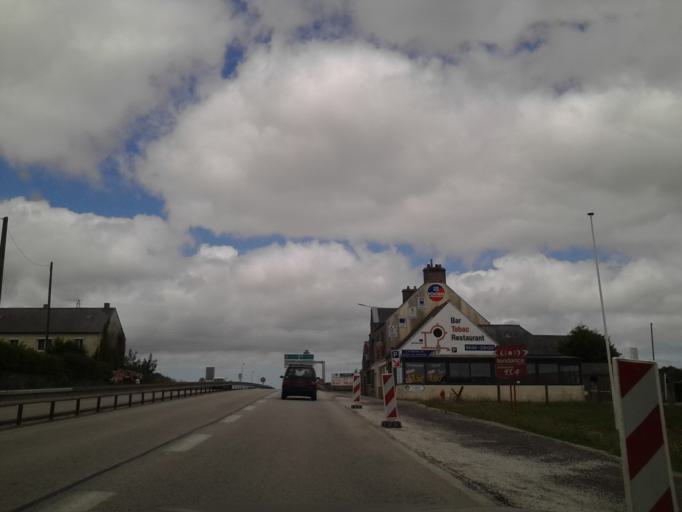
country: FR
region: Lower Normandy
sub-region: Departement de la Manche
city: La Glacerie
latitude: 49.5952
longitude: -1.5959
